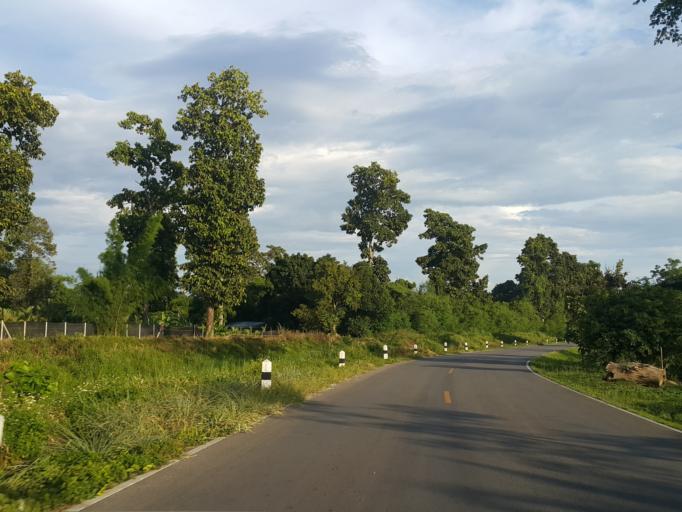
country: TH
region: Chiang Mai
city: San Sai
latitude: 18.8970
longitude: 99.0211
